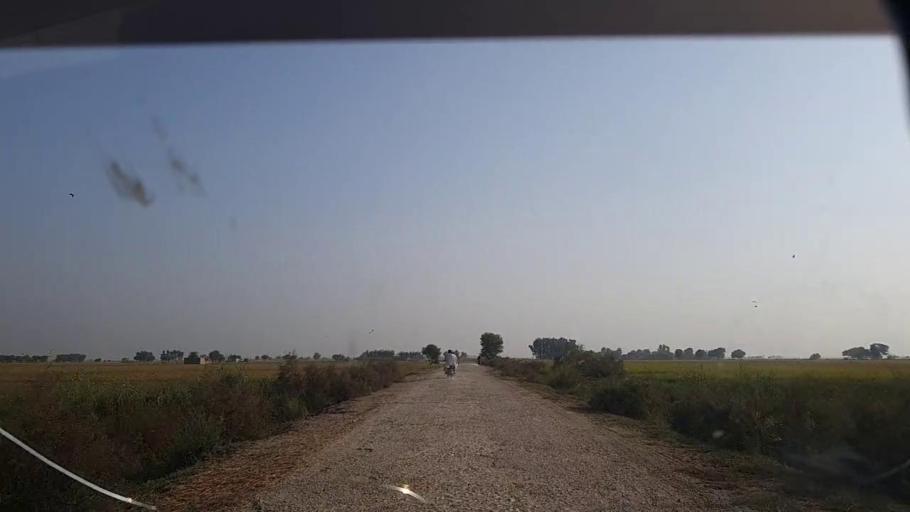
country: PK
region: Sindh
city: Shikarpur
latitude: 28.0679
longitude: 68.5463
